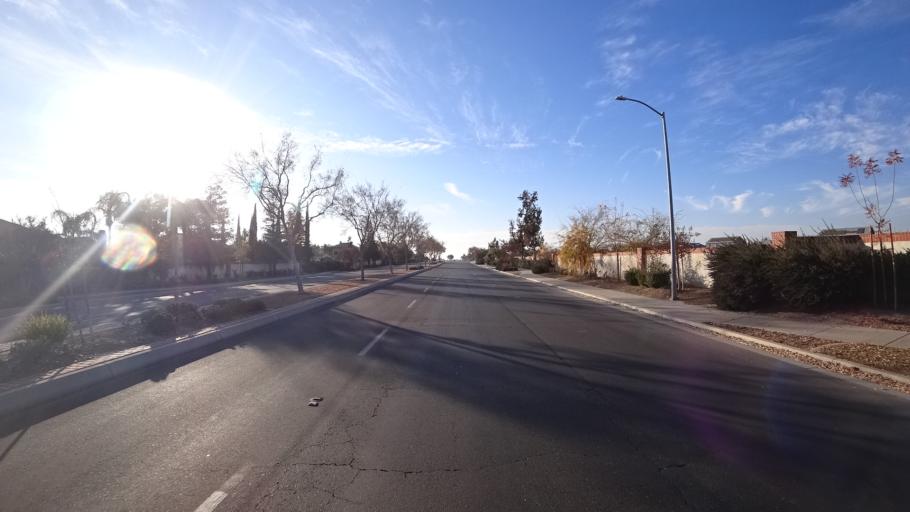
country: US
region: California
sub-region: Kern County
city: Rosedale
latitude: 35.3400
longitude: -119.1365
